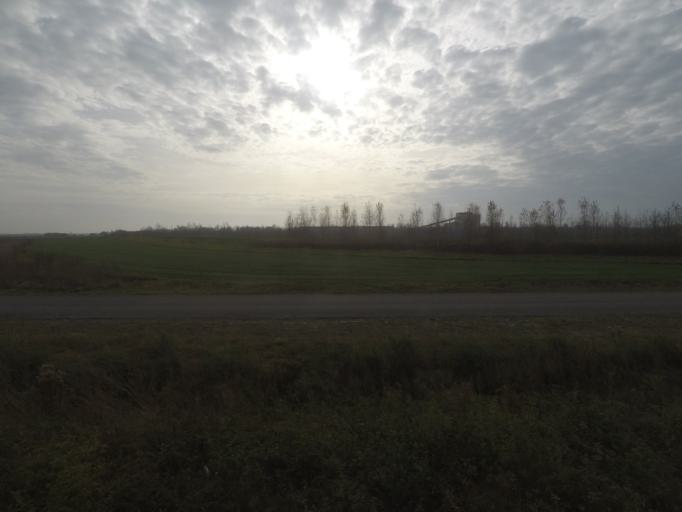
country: PL
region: Subcarpathian Voivodeship
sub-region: Powiat ropczycko-sedziszowski
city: Ostrow
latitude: 50.0797
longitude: 21.6054
